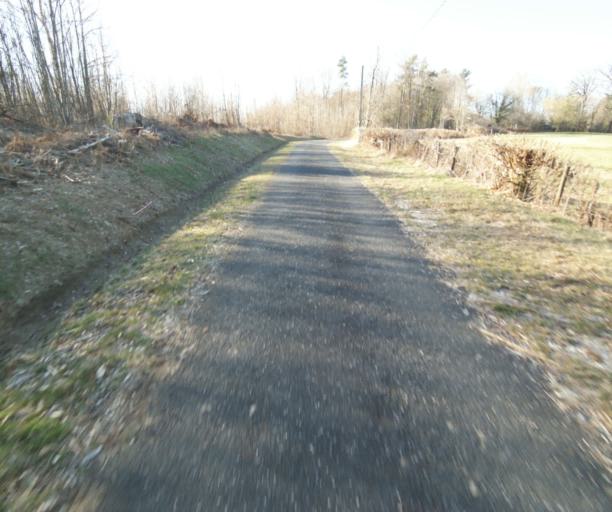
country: FR
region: Limousin
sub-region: Departement de la Correze
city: Seilhac
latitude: 45.3861
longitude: 1.6987
